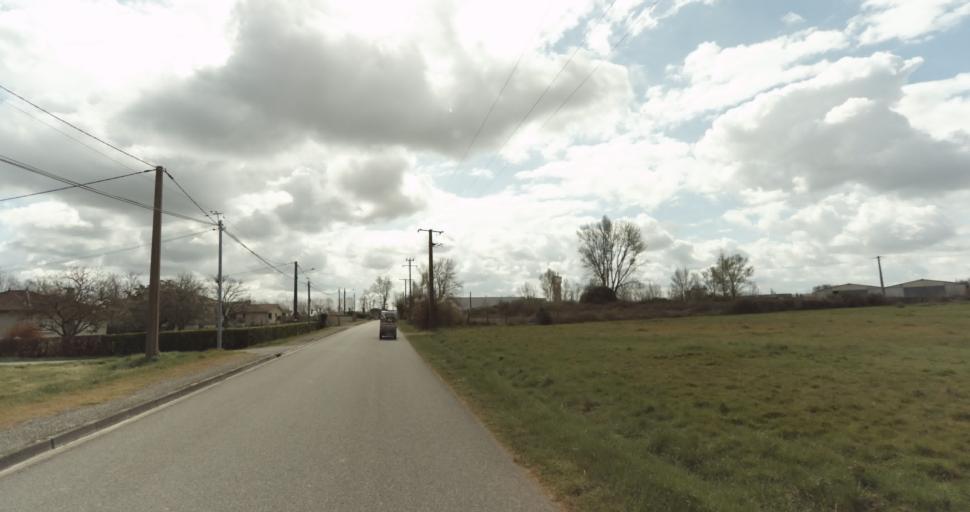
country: FR
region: Midi-Pyrenees
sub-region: Departement de la Haute-Garonne
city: Auterive
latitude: 43.3644
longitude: 1.4630
